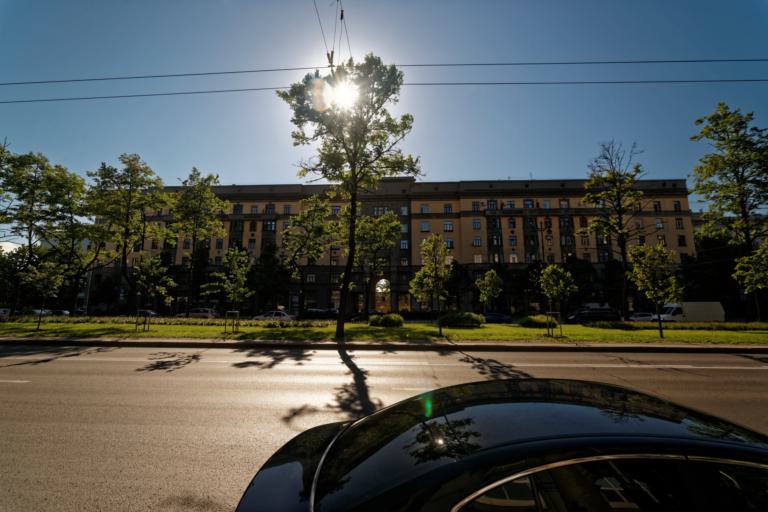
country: RU
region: St.-Petersburg
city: Admiralteisky
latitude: 59.8999
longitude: 30.3194
